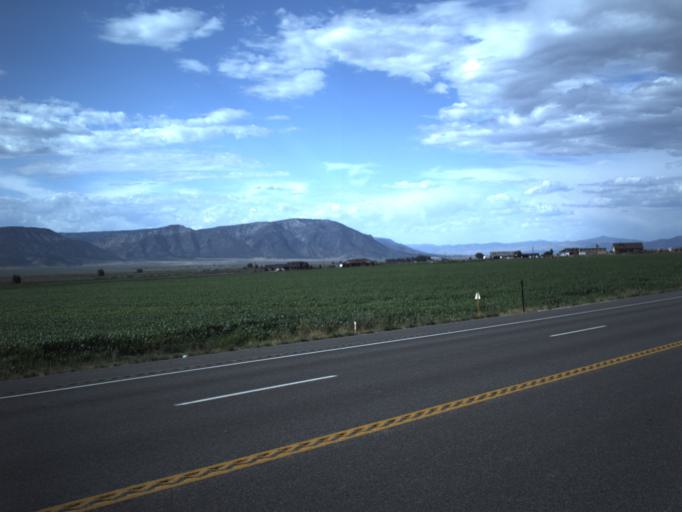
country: US
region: Utah
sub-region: Sanpete County
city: Manti
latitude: 39.3000
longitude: -111.6185
